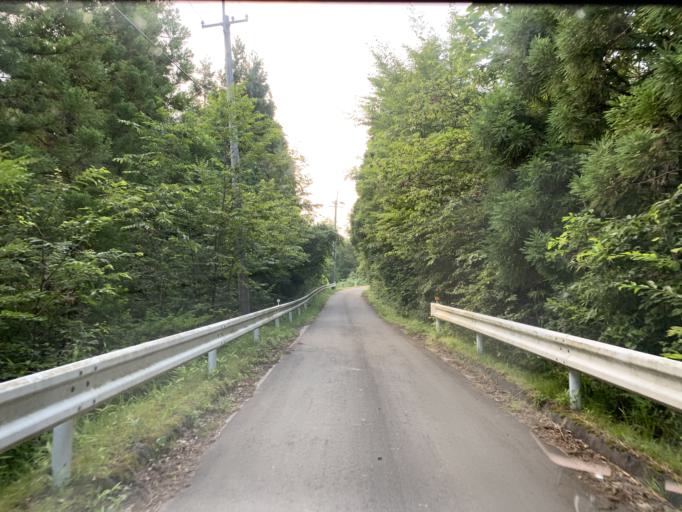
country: JP
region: Iwate
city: Ichinoseki
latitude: 38.8329
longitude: 141.1498
